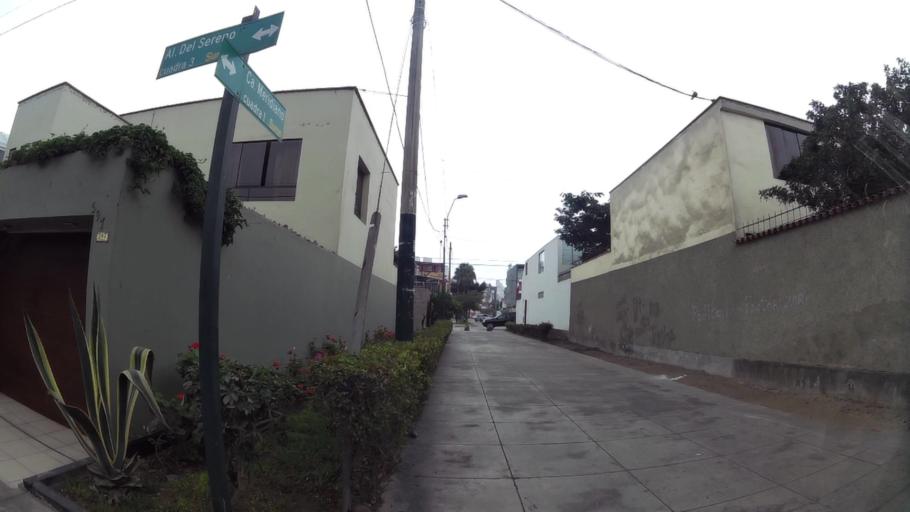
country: PE
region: Lima
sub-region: Lima
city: Surco
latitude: -12.1248
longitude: -76.9890
